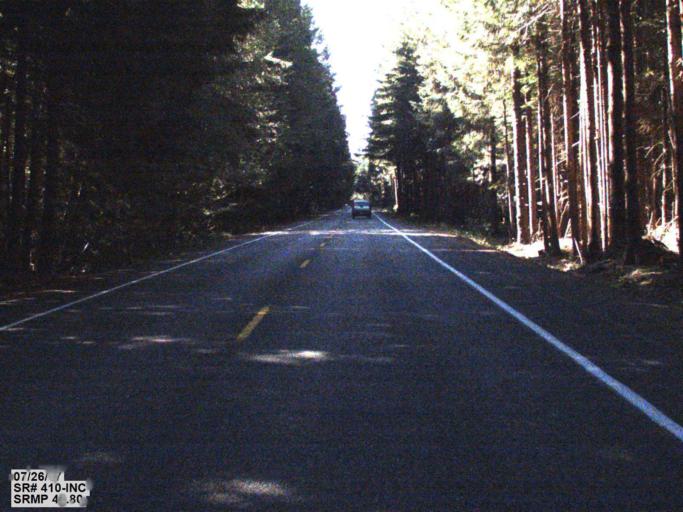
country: US
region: Washington
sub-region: King County
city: Riverbend
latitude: 47.1263
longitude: -121.6156
